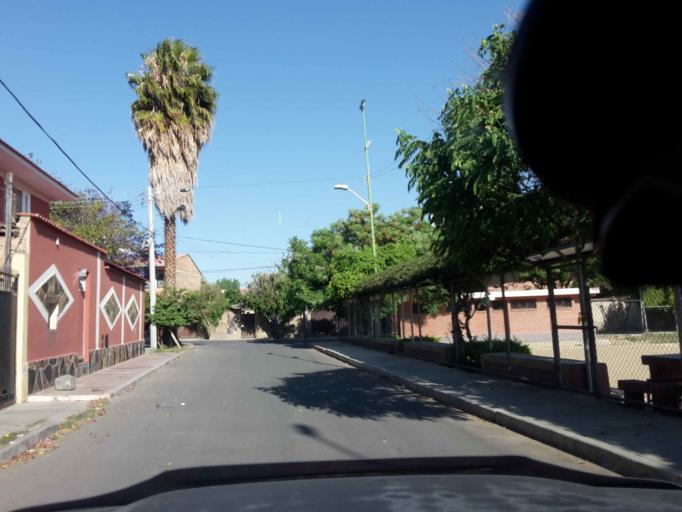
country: BO
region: Cochabamba
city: Cochabamba
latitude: -17.3678
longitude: -66.1836
